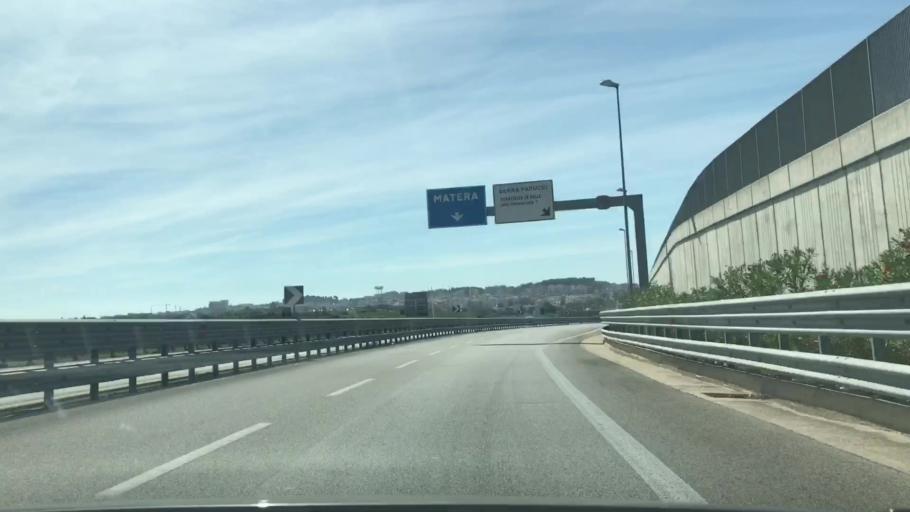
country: IT
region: Basilicate
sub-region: Provincia di Matera
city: Matera
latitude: 40.6934
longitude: 16.5912
